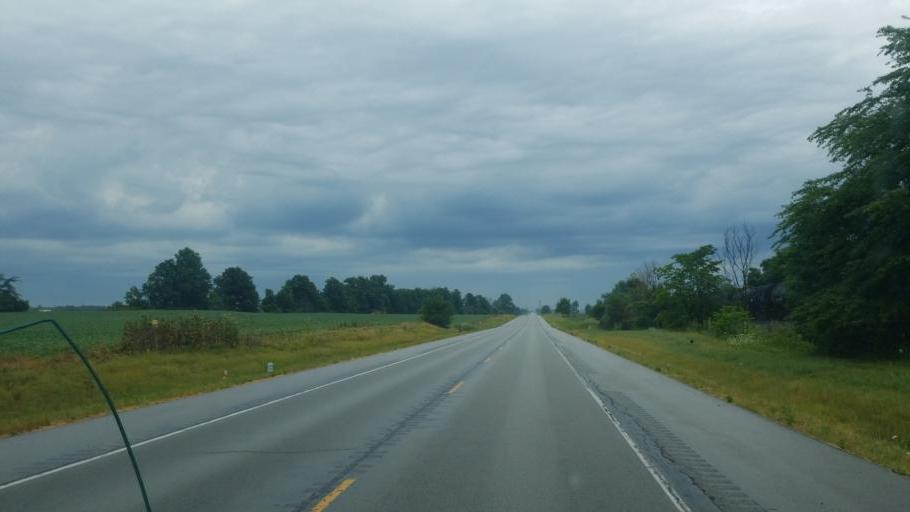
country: US
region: Indiana
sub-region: DeKalb County
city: Butler
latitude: 41.4359
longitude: -84.8210
